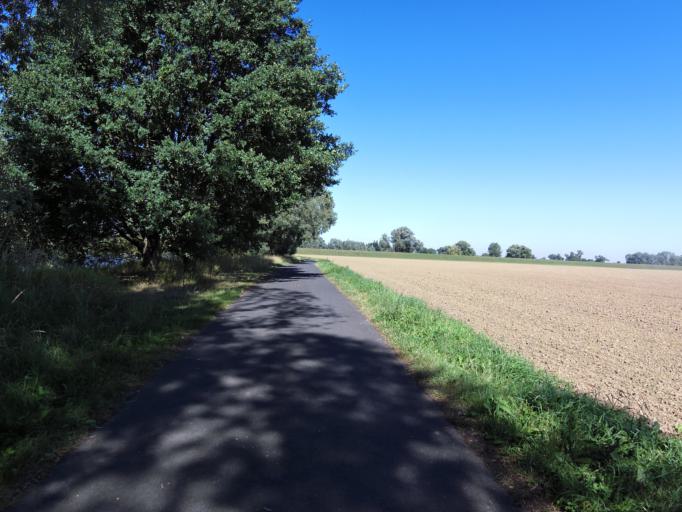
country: DE
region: Saxony-Anhalt
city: Pretzsch
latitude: 51.7064
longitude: 12.8199
